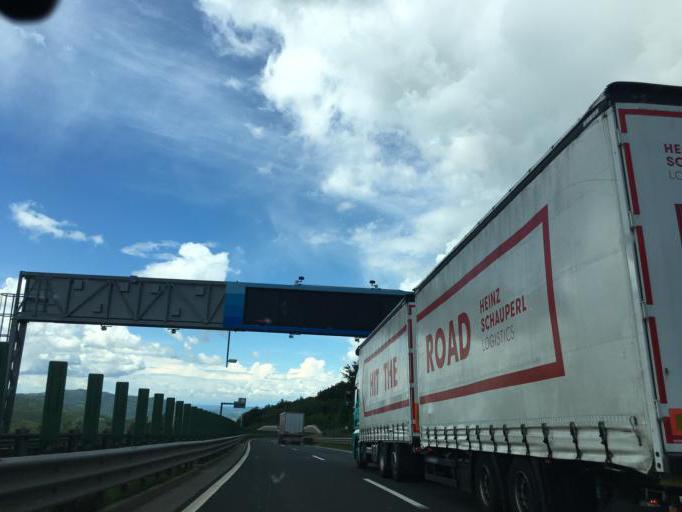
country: SI
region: Divaca
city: Divaca
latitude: 45.7619
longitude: 14.0422
